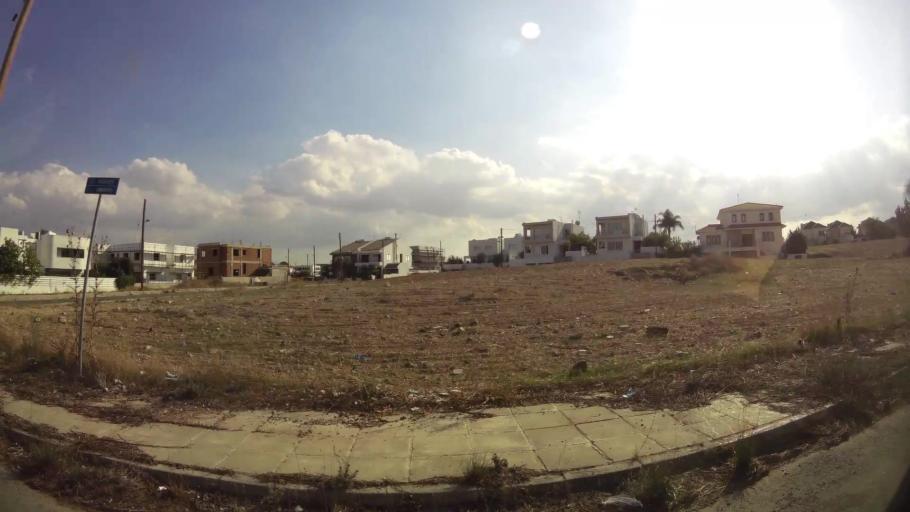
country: CY
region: Lefkosia
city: Kato Deftera
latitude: 35.1377
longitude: 33.2985
